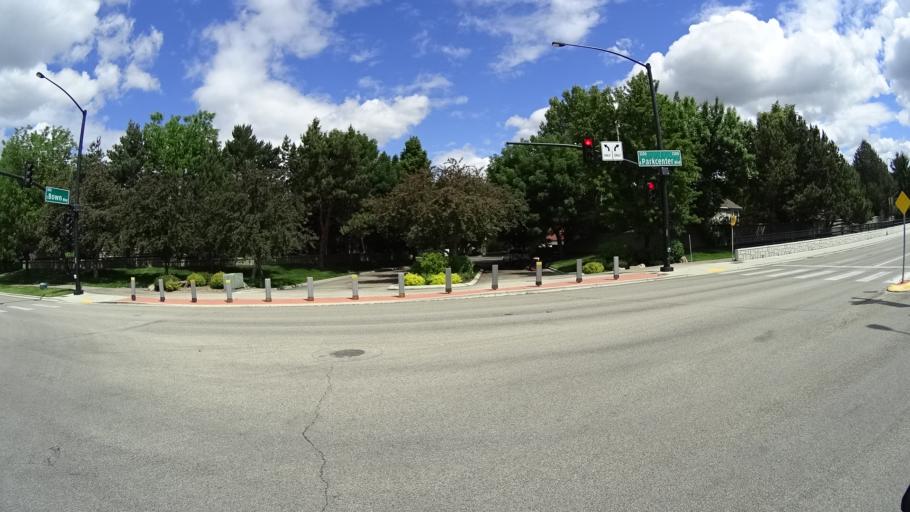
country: US
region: Idaho
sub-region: Ada County
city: Boise
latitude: 43.5753
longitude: -116.1541
